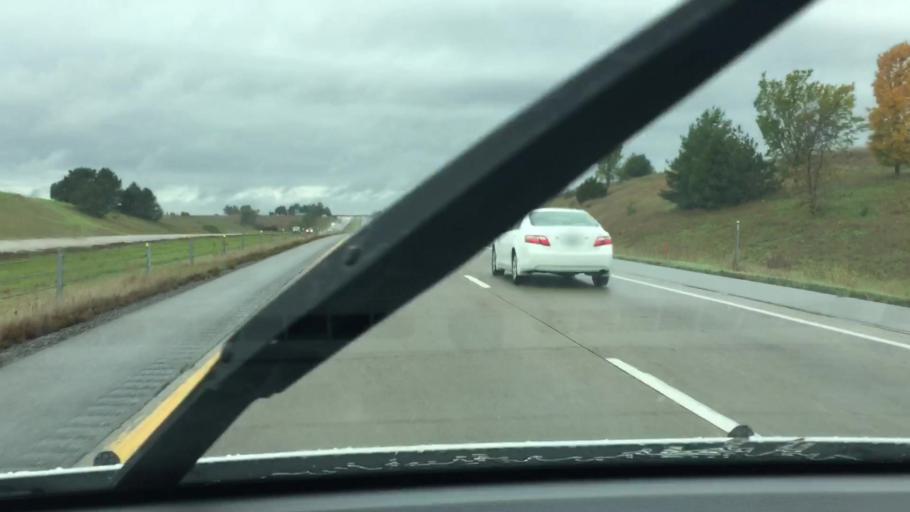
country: US
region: Iowa
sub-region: Poweshiek County
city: Brooklyn
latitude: 41.6963
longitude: -92.3799
